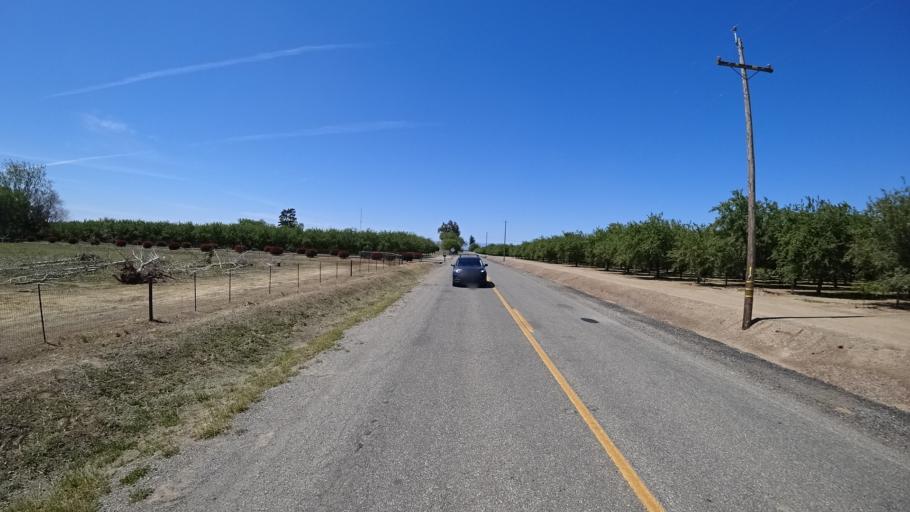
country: US
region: California
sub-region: Glenn County
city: Orland
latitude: 39.7248
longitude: -122.1059
